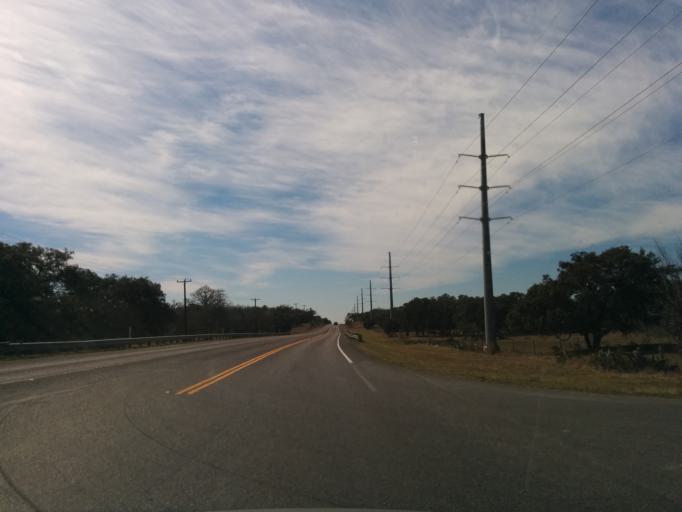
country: US
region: Texas
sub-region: Bexar County
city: Fair Oaks Ranch
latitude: 29.7702
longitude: -98.6049
